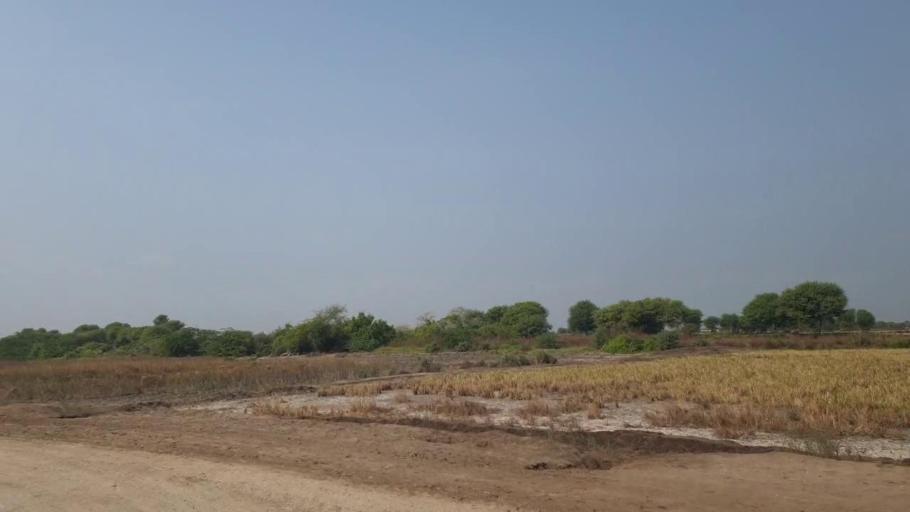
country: PK
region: Sindh
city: Badin
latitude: 24.5467
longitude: 68.6596
